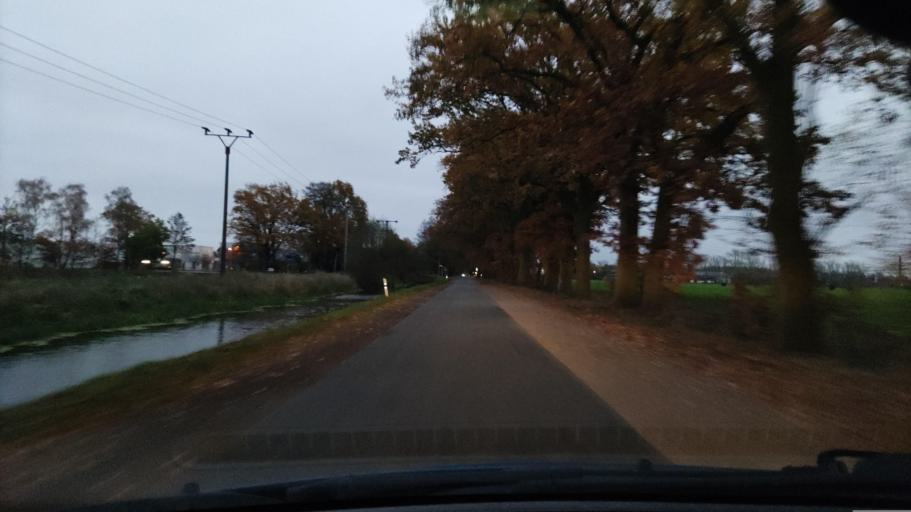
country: DE
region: Mecklenburg-Vorpommern
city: Neu Kaliss
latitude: 53.1815
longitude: 11.2718
